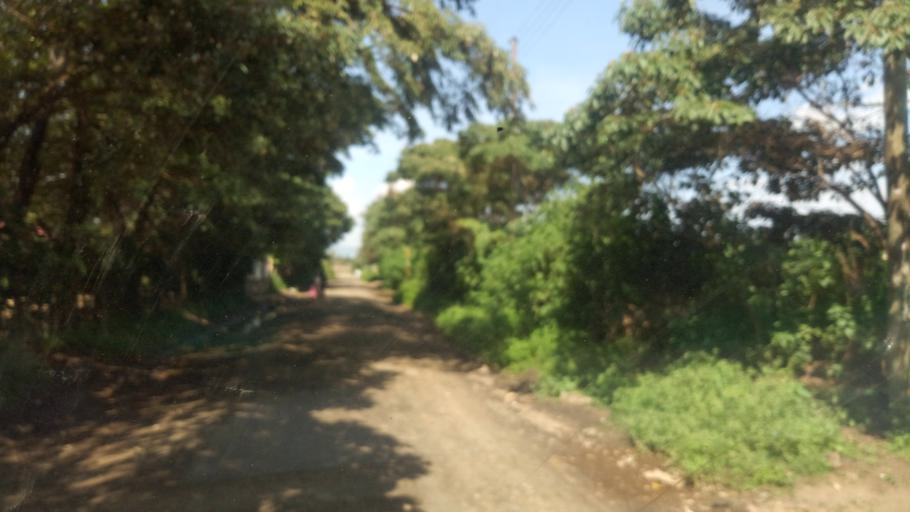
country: KE
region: Nakuru
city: Nakuru
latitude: -0.2773
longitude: 36.1150
